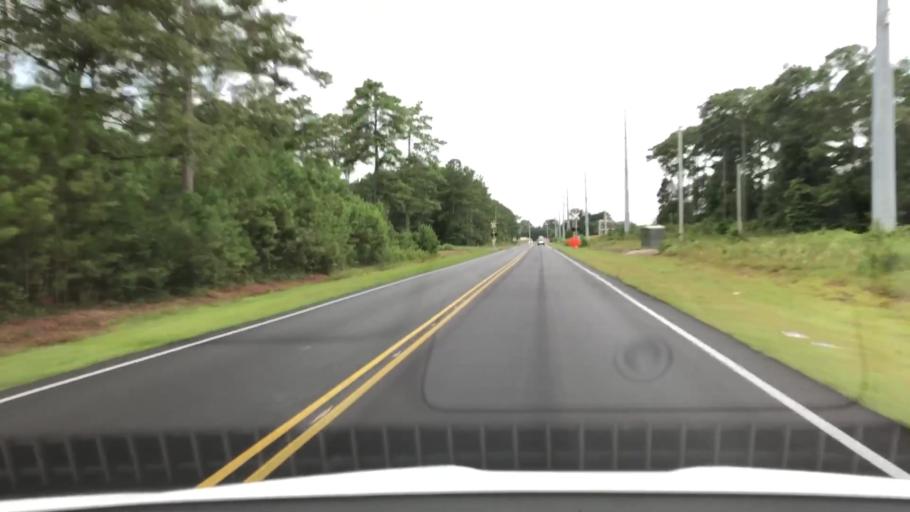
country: US
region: North Carolina
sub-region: Onslow County
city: Swansboro
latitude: 34.7869
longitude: -77.1203
